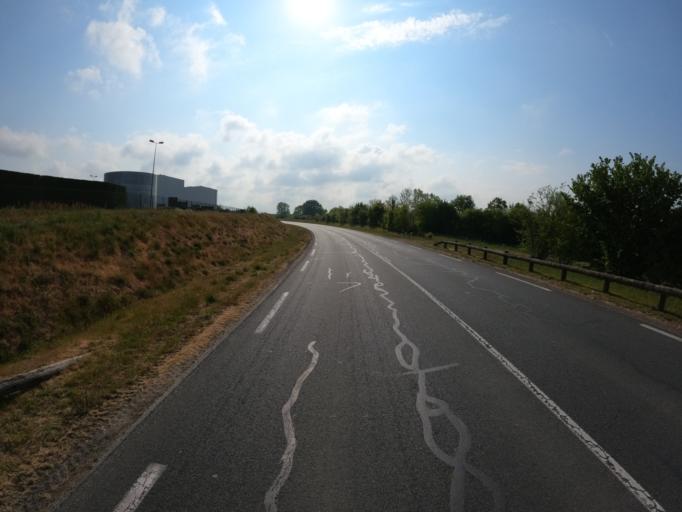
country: FR
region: Pays de la Loire
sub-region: Departement de la Vendee
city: La Bruffiere
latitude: 47.0066
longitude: -1.1974
